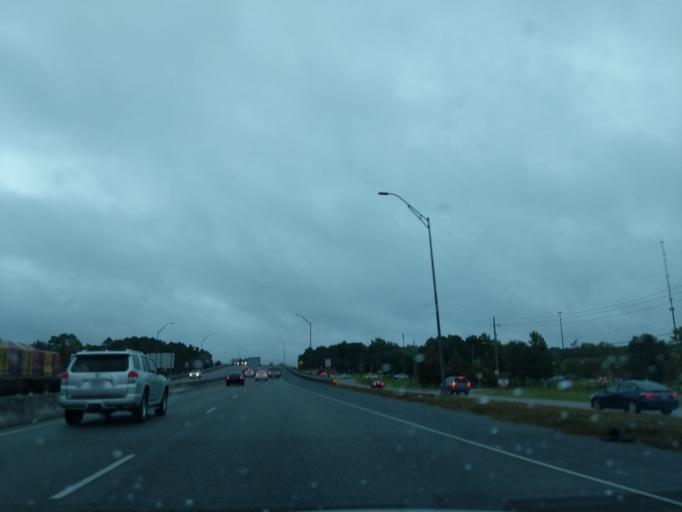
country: US
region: Texas
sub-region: Angelina County
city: Lufkin
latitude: 31.3340
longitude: -94.6899
